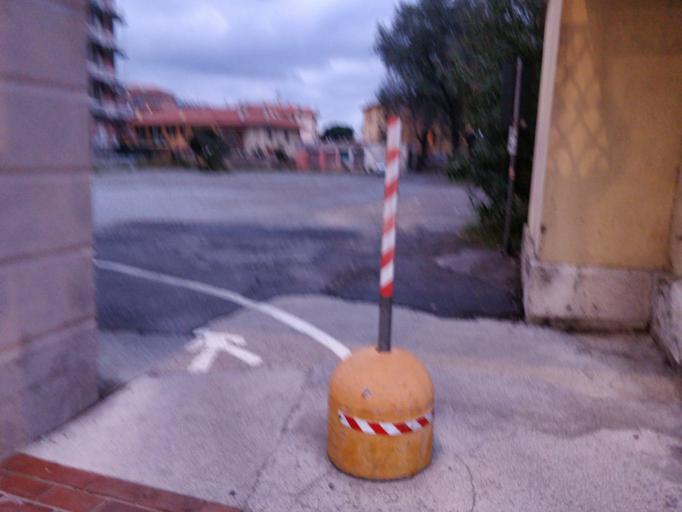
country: IT
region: Liguria
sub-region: Provincia di Savona
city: Andora
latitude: 43.9493
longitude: 8.1413
